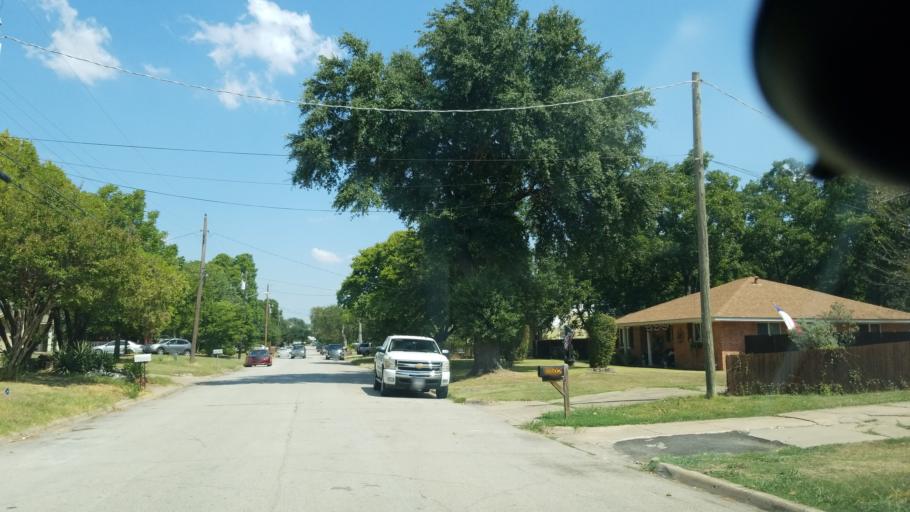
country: US
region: Texas
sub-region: Dallas County
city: Grand Prairie
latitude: 32.7120
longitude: -96.9891
